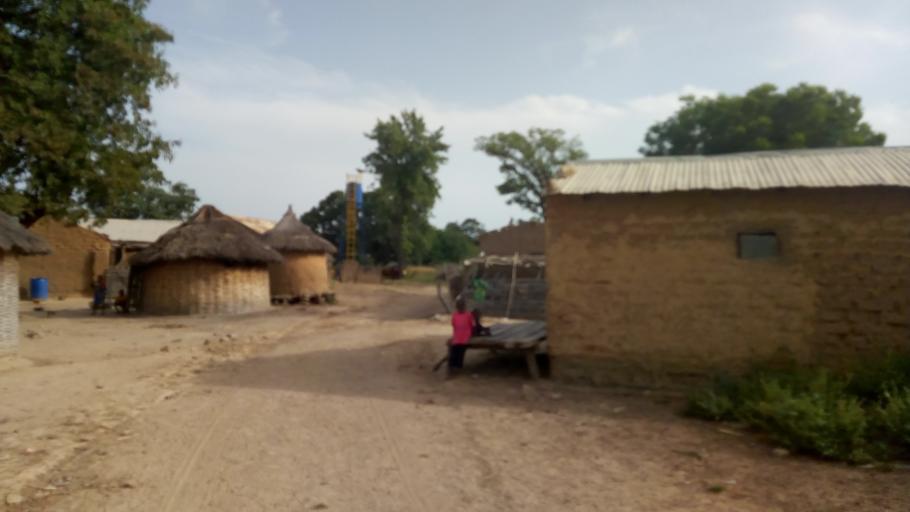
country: ML
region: Kayes
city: Kita
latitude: 13.1615
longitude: -8.9338
